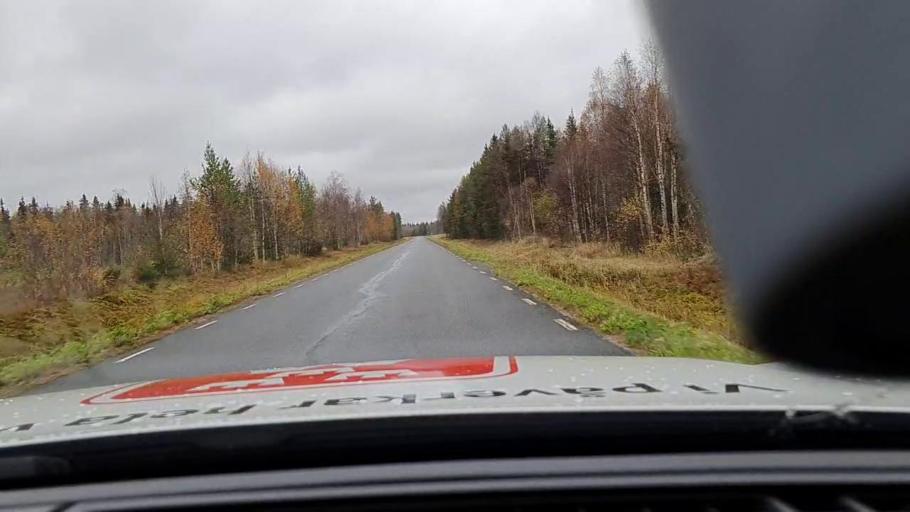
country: SE
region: Norrbotten
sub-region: Haparanda Kommun
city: Haparanda
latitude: 65.9282
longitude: 23.8181
